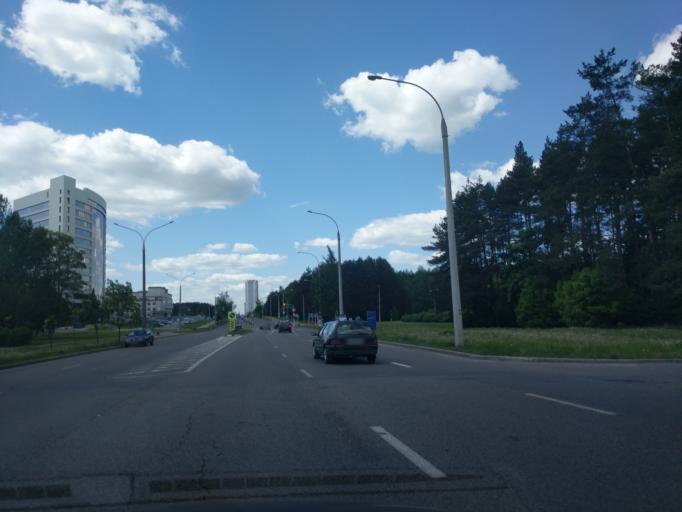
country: BY
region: Minsk
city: Borovlyany
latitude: 53.9244
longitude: 27.6687
